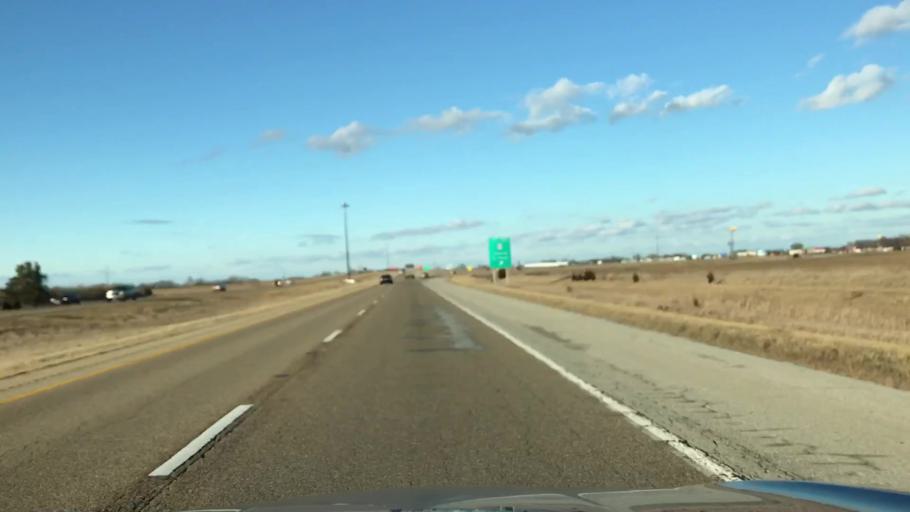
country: US
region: Illinois
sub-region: McLean County
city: Chenoa
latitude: 40.7339
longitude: -88.7374
